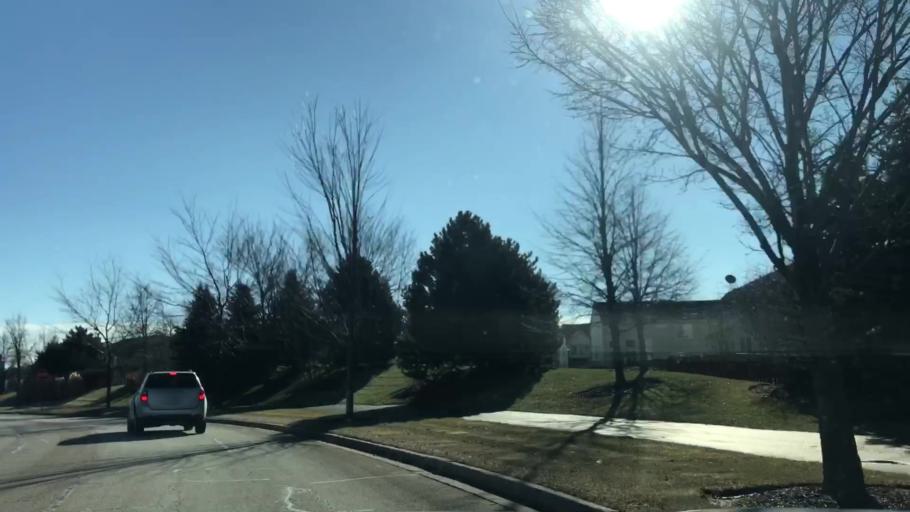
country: US
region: Illinois
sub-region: Kane County
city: Pingree Grove
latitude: 42.0815
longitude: -88.4313
